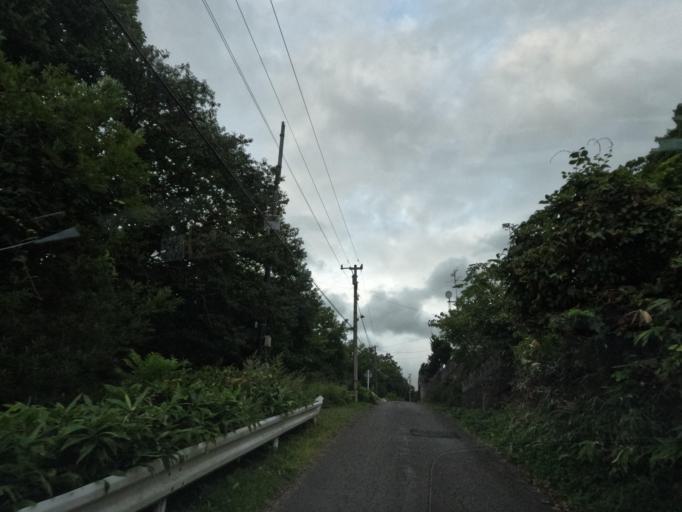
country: JP
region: Hokkaido
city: Muroran
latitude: 42.3680
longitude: 140.9658
